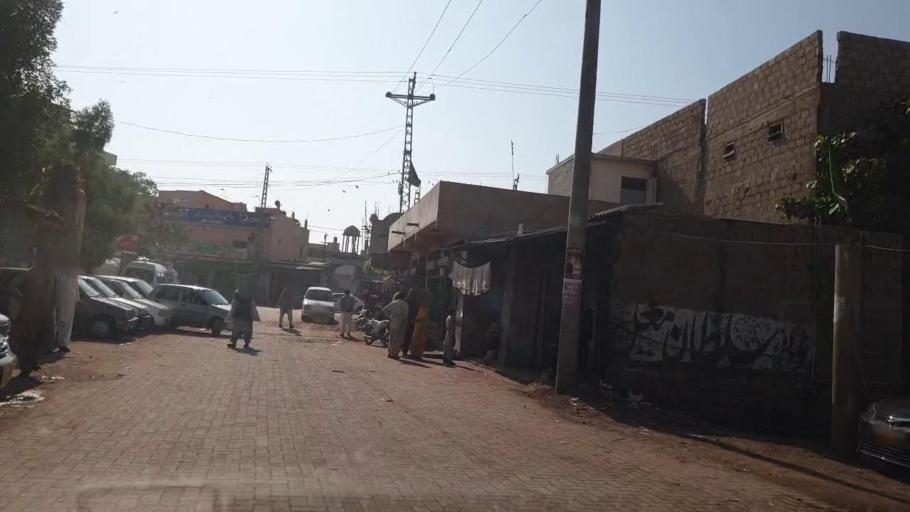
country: PK
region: Sindh
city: Thatta
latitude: 24.7517
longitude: 67.9203
